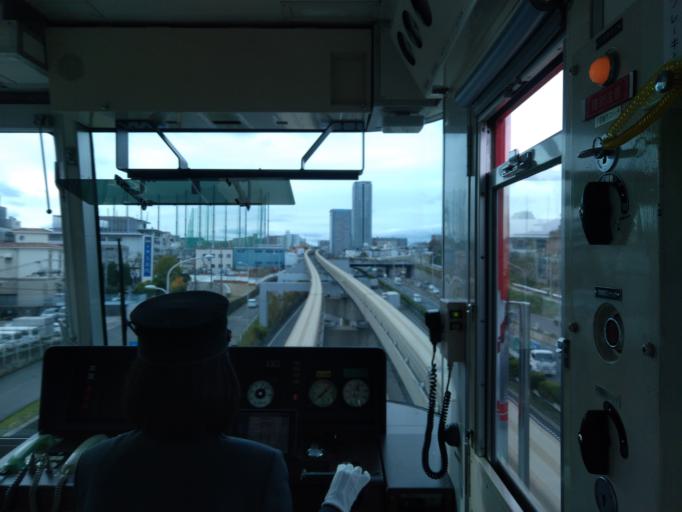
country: JP
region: Osaka
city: Mino
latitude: 34.8066
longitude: 135.5065
